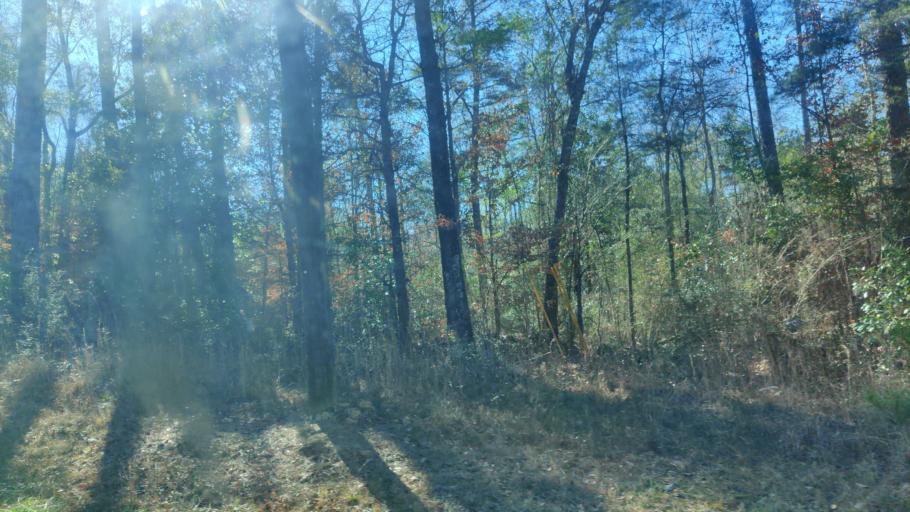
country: US
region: Mississippi
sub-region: Jones County
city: Ellisville
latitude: 31.5545
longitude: -89.3287
